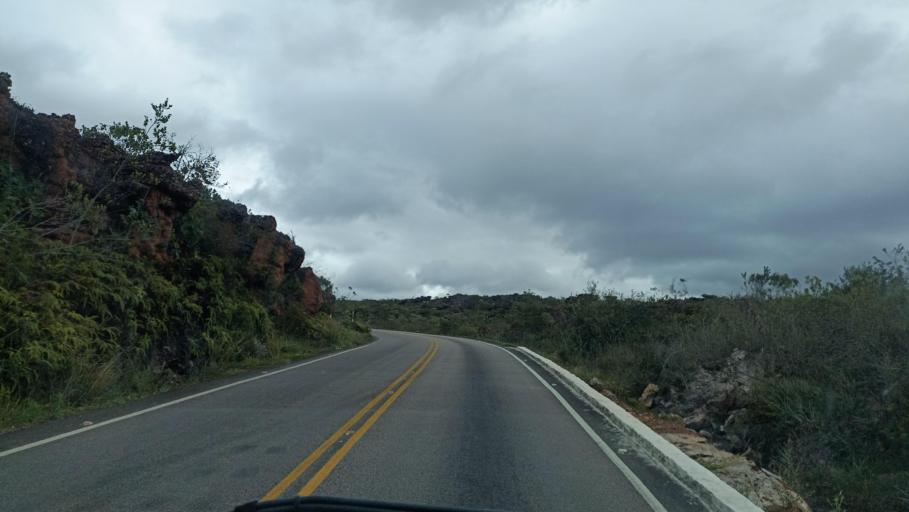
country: BR
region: Bahia
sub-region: Andarai
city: Vera Cruz
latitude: -12.9923
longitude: -41.3573
